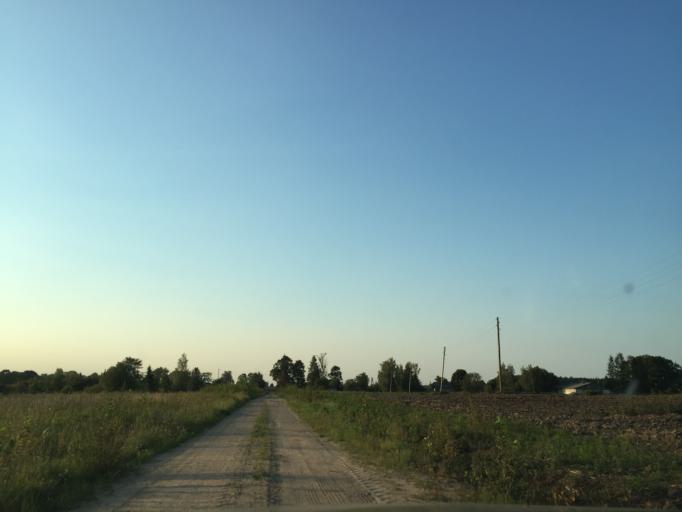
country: LV
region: Limbazu Rajons
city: Limbazi
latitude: 57.5686
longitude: 24.7712
